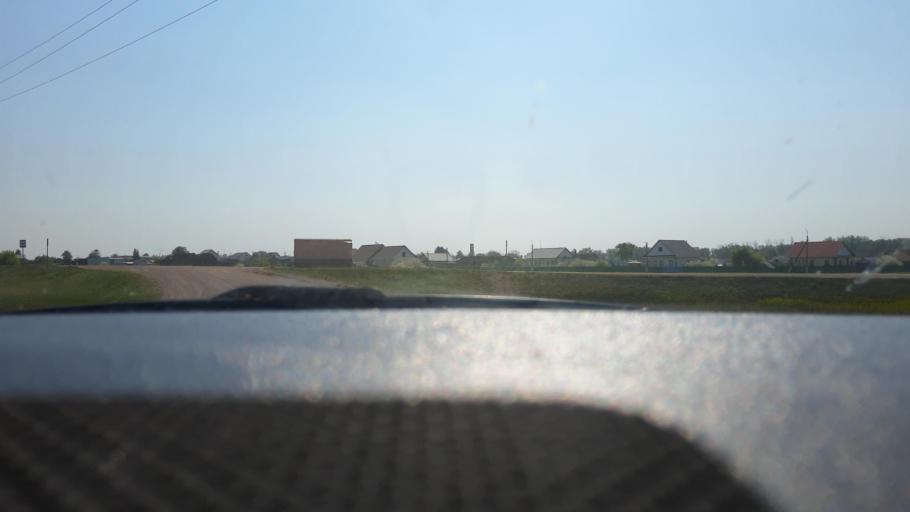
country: RU
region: Bashkortostan
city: Chishmy
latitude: 54.4306
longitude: 55.2921
